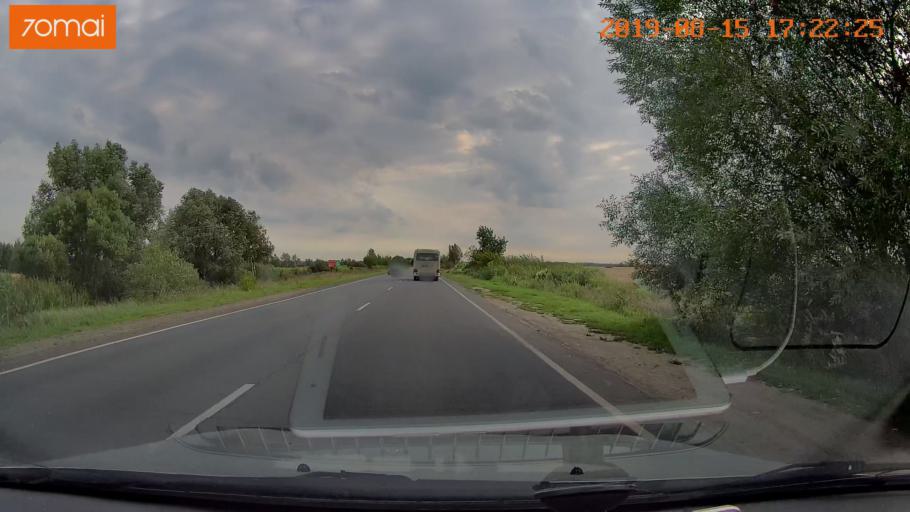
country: RU
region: Moskovskaya
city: Ashitkovo
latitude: 55.4146
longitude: 38.5625
